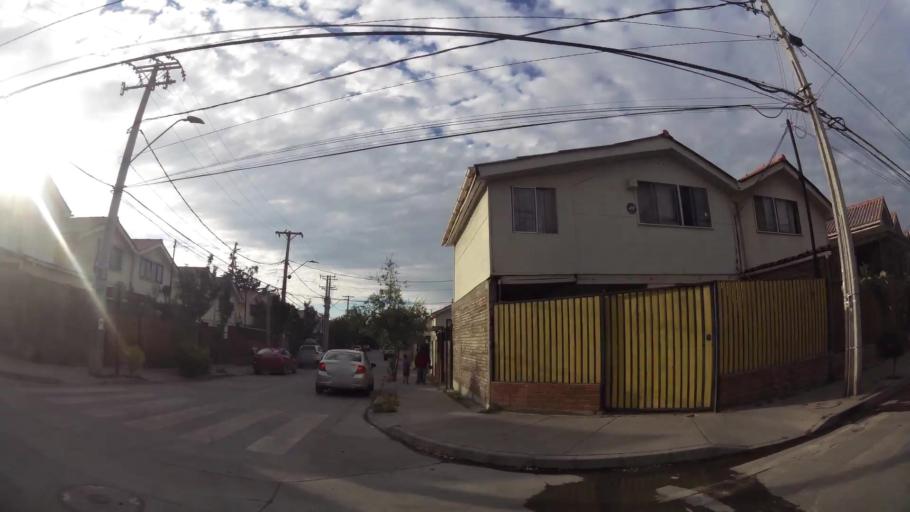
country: CL
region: Santiago Metropolitan
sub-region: Provincia de Maipo
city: San Bernardo
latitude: -33.6466
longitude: -70.6641
